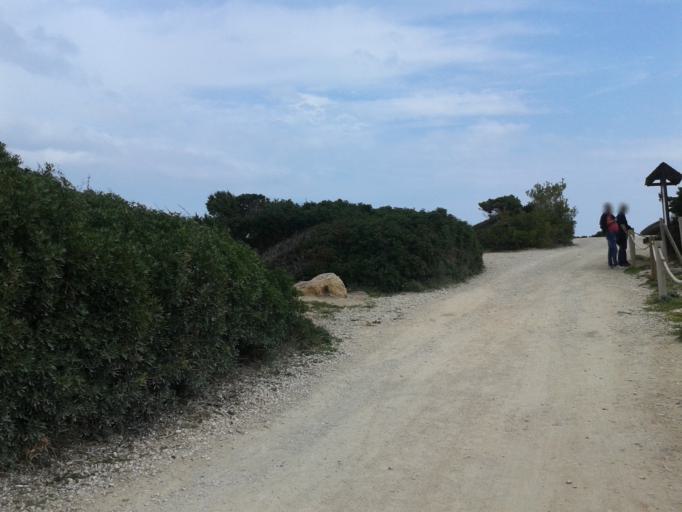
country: ES
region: Balearic Islands
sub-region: Illes Balears
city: Son Servera
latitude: 39.5849
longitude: 3.3910
